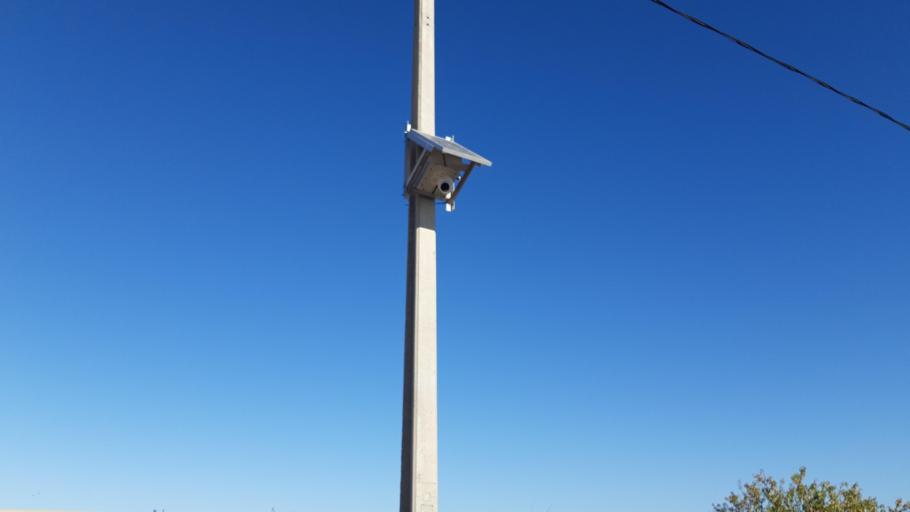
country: TN
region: Safaqis
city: Sfax
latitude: 34.8422
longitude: 10.7224
